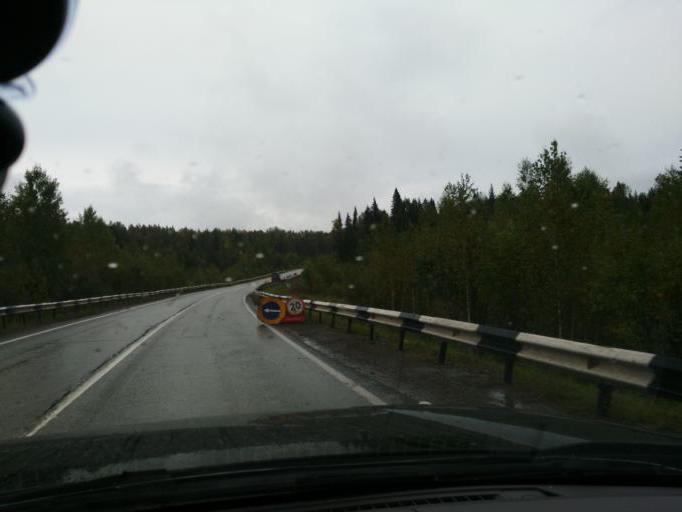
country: RU
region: Perm
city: Yugo-Kamskiy
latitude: 57.7496
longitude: 55.7121
